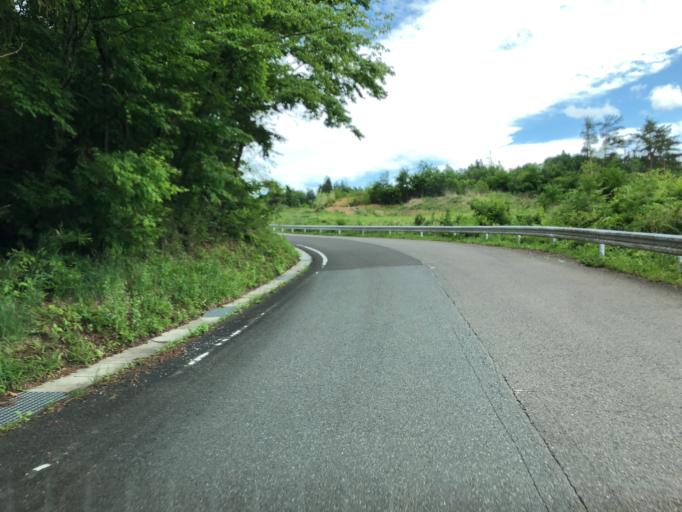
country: JP
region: Fukushima
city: Nihommatsu
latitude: 37.6346
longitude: 140.5039
